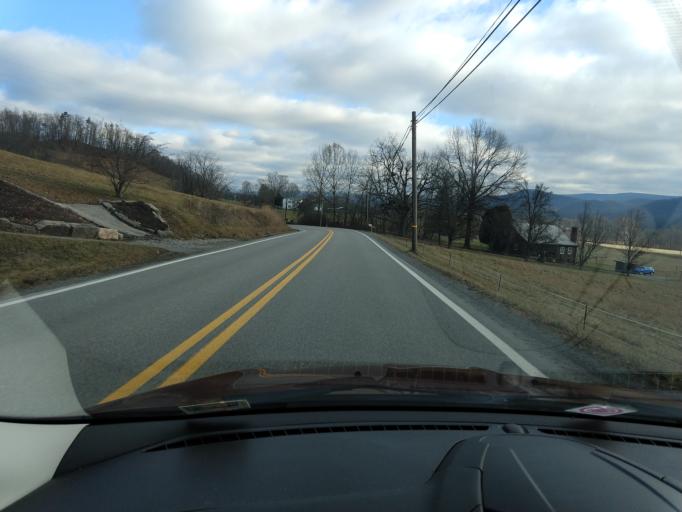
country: US
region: West Virginia
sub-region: Randolph County
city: Elkins
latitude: 38.7791
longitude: -79.9157
